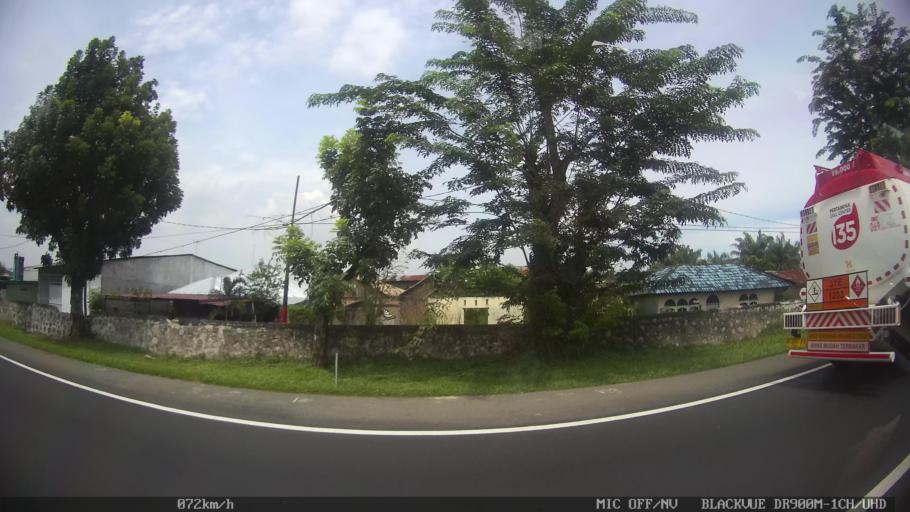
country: ID
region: North Sumatra
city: Labuhan Deli
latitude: 3.7196
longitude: 98.6827
